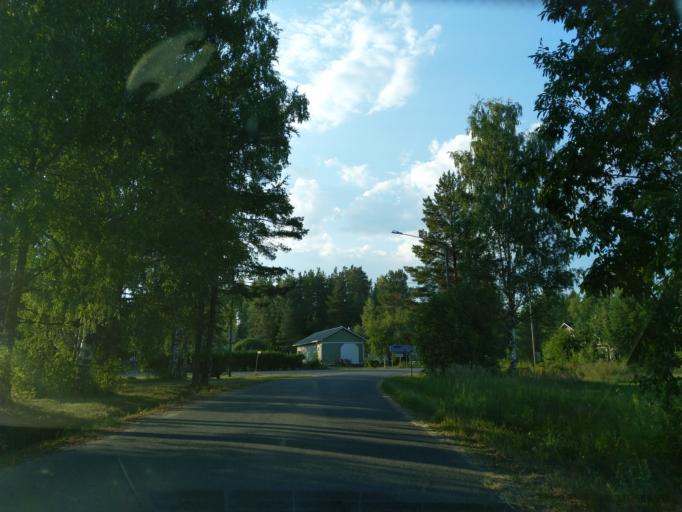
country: FI
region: Satakunta
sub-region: Pohjois-Satakunta
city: Honkajoki
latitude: 61.8203
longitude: 22.1992
